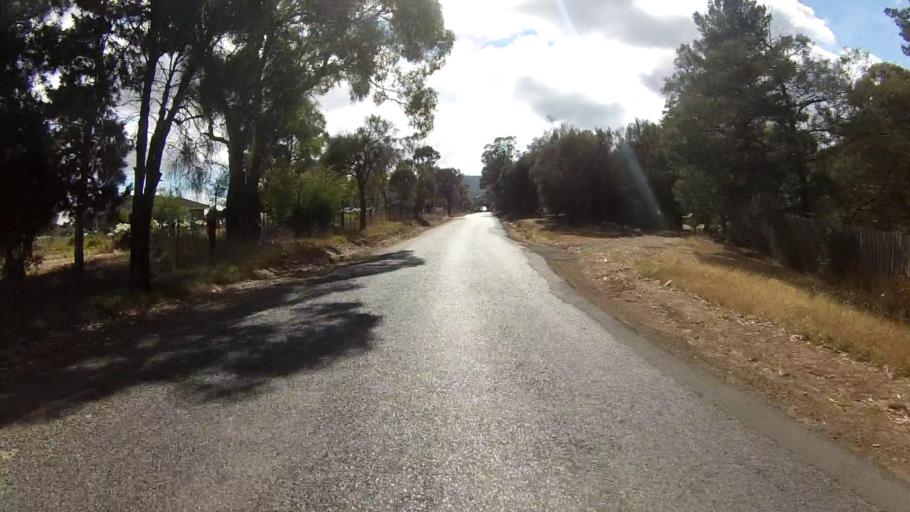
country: AU
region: Tasmania
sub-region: Brighton
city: Old Beach
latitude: -42.7722
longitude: 147.2889
